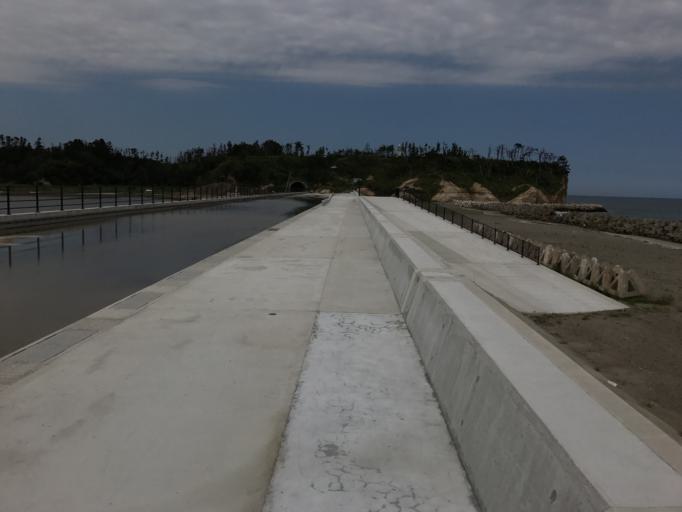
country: JP
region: Miyagi
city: Marumori
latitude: 37.8196
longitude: 140.9857
